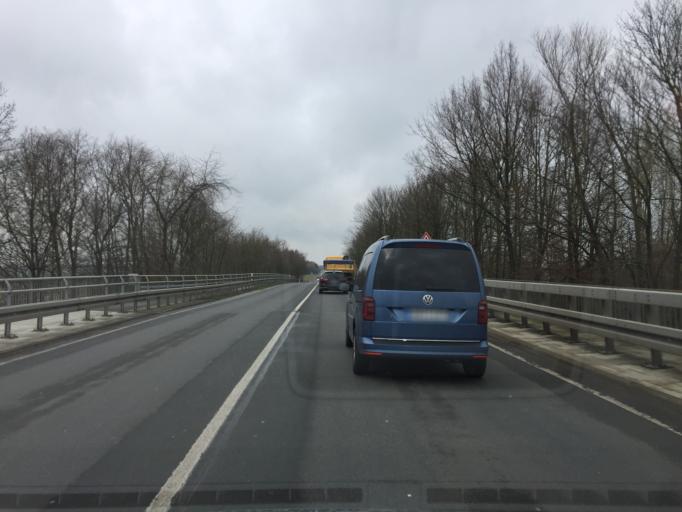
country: DE
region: Lower Saxony
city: Wunstorf
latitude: 52.4005
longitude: 9.4631
